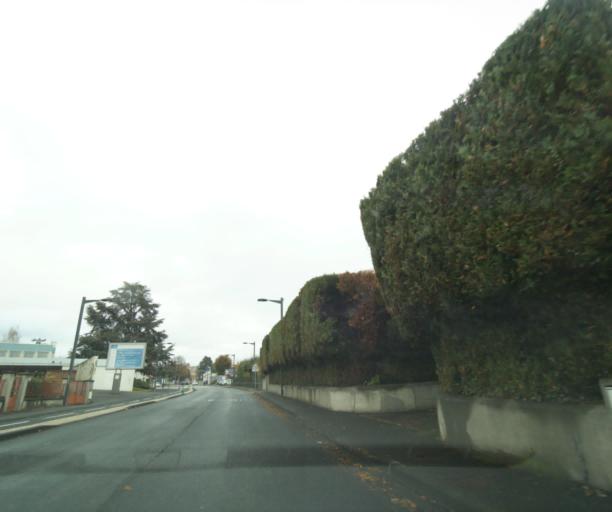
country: FR
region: Auvergne
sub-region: Departement du Puy-de-Dome
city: Cournon-d'Auvergne
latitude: 45.7370
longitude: 3.1942
